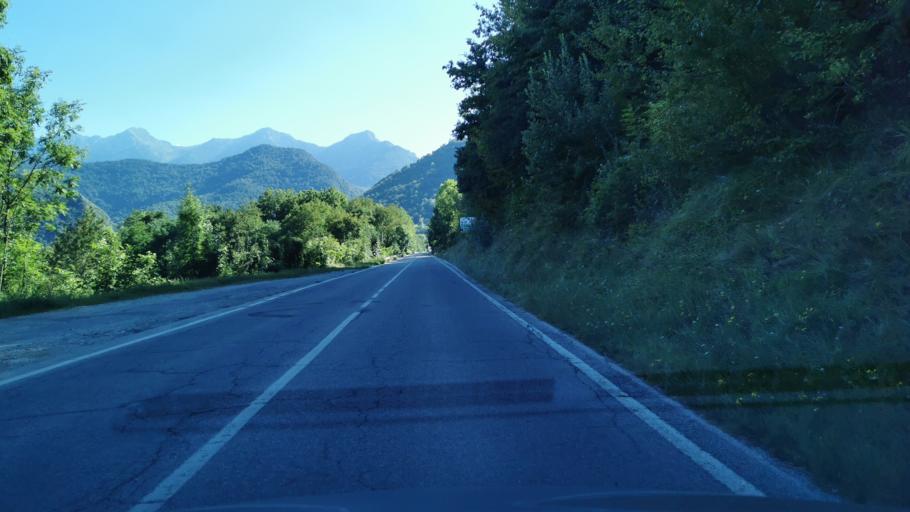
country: IT
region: Piedmont
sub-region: Provincia di Cuneo
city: Roccavione
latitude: 44.3133
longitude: 7.4592
